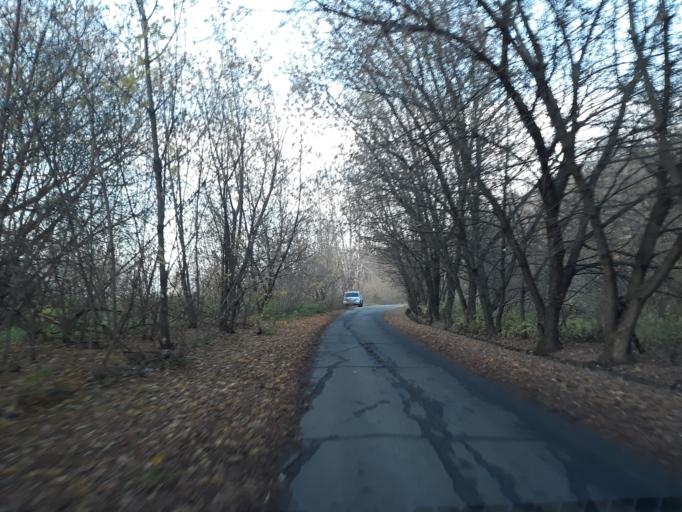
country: RU
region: Nizjnij Novgorod
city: Nizhniy Novgorod
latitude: 56.2810
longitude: 43.9697
